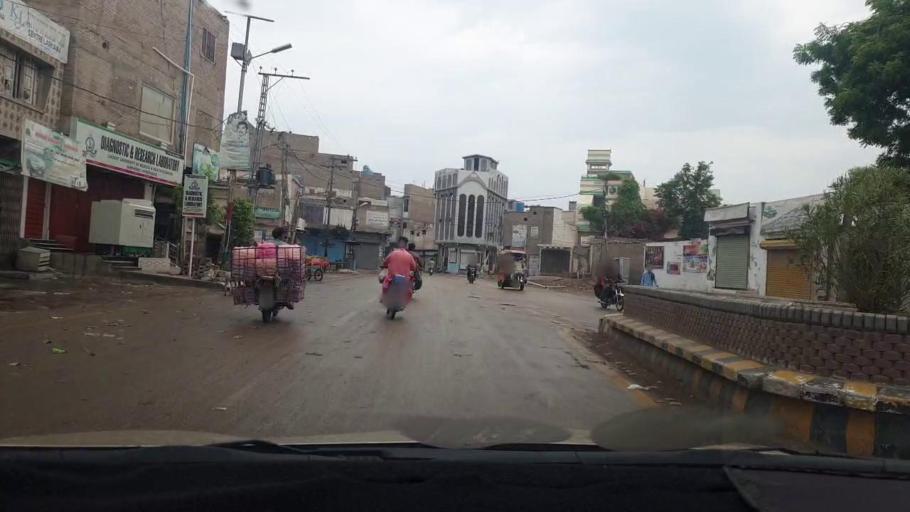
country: PK
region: Sindh
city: Larkana
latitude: 27.5582
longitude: 68.2095
